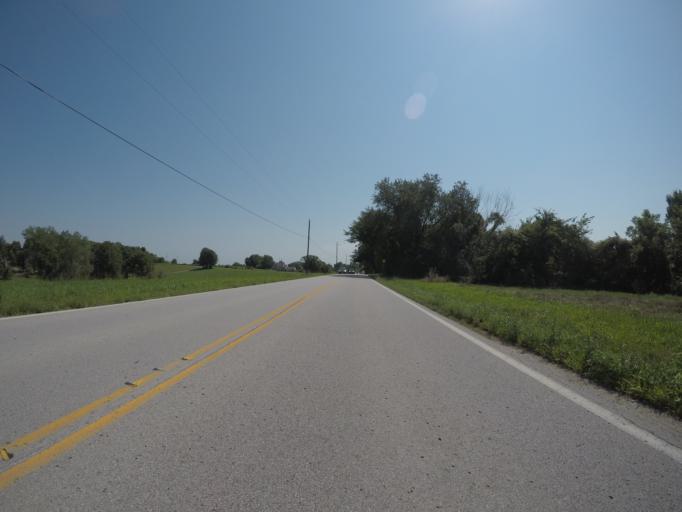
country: US
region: Kansas
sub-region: Leavenworth County
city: Lansing
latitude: 39.2433
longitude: -94.8721
